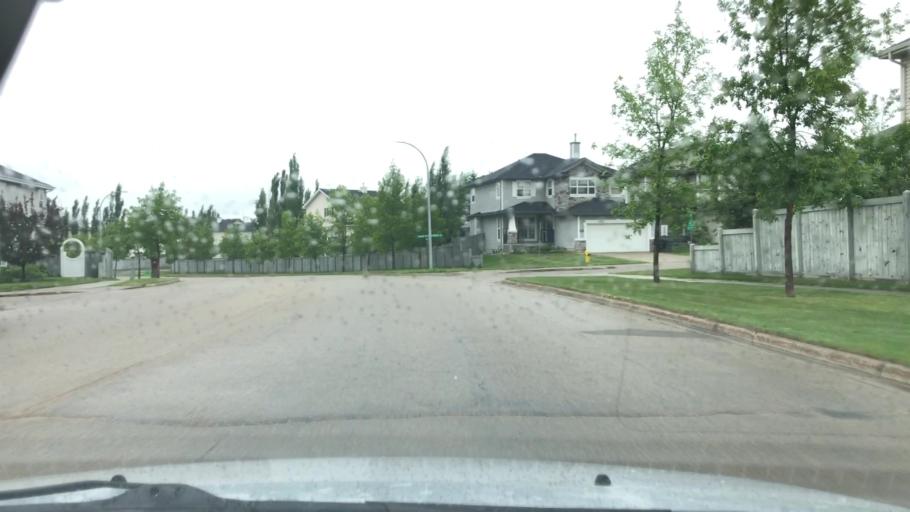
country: CA
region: Alberta
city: Sherwood Park
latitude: 53.5367
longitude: -113.2604
